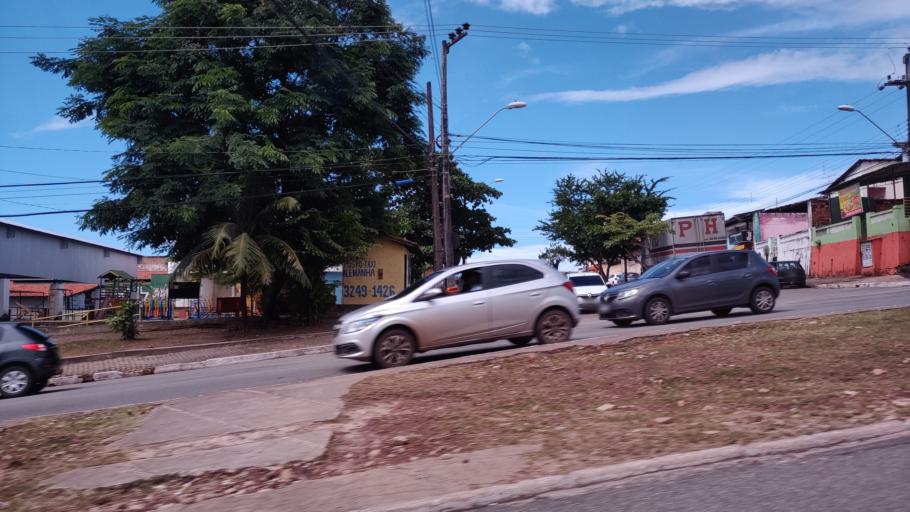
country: BR
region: Maranhao
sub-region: Sao Luis
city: Sao Luis
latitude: -2.5380
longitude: -44.2701
